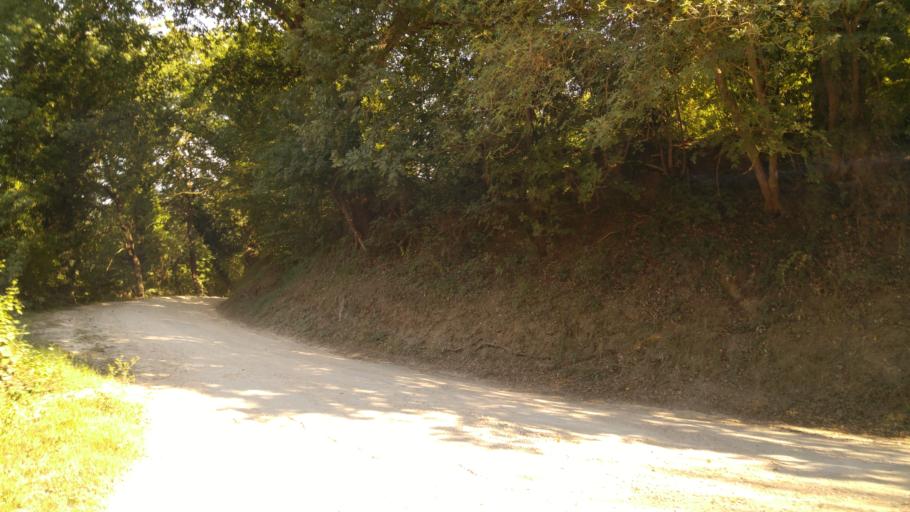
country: IT
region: The Marches
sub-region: Provincia di Pesaro e Urbino
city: Fossombrone
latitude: 43.6803
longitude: 12.7887
